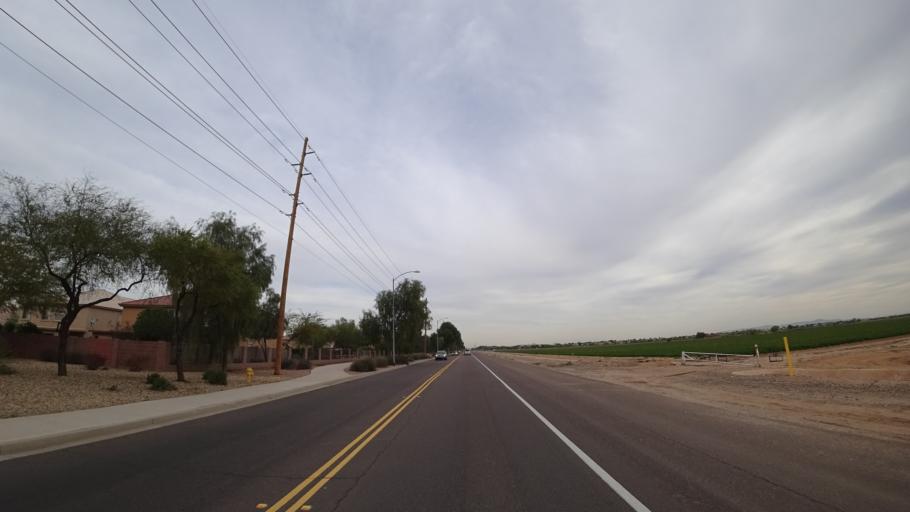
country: US
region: Arizona
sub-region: Maricopa County
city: Surprise
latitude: 33.6097
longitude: -112.4023
